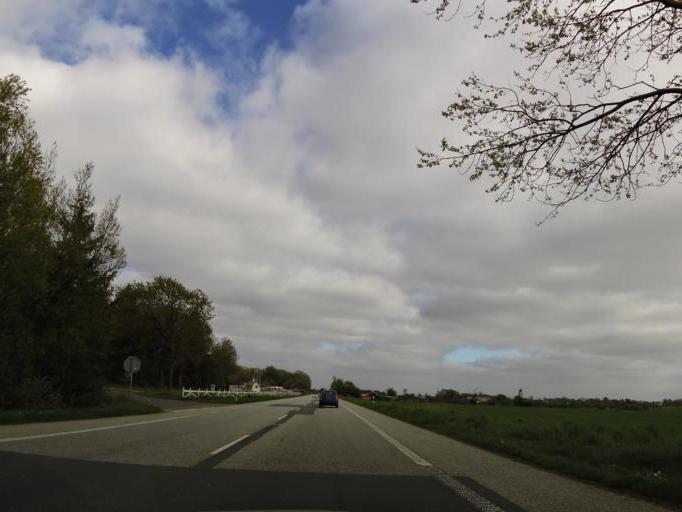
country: DE
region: Schleswig-Holstein
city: Risum-Lindholm
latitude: 54.7689
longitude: 8.8633
